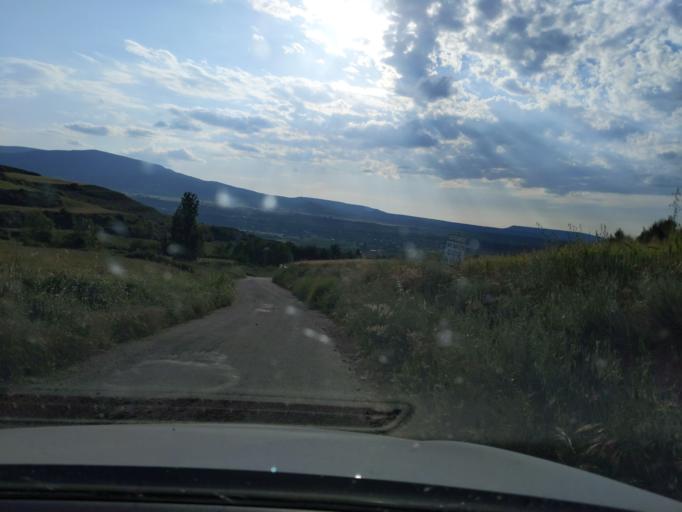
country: ES
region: La Rioja
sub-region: Provincia de La Rioja
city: Albelda de Iregua
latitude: 42.3538
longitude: -2.4614
